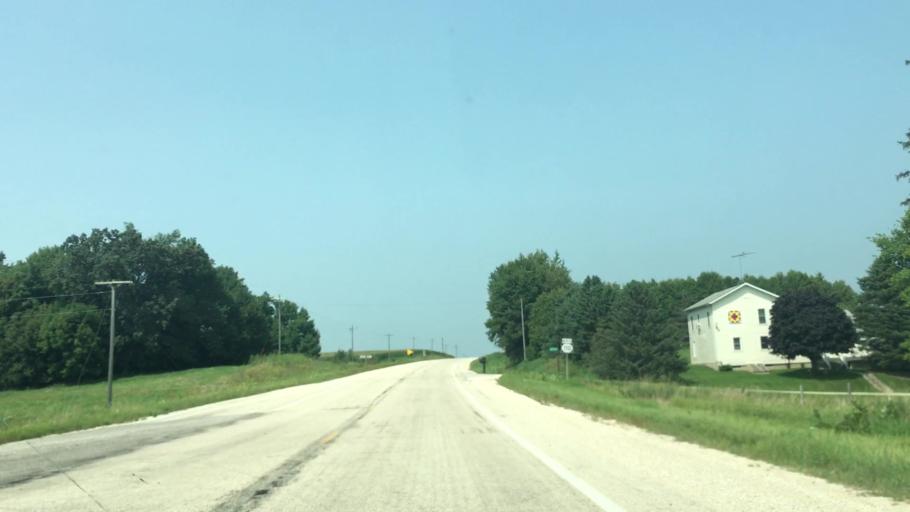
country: US
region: Iowa
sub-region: Fayette County
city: West Union
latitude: 43.0036
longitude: -91.8244
